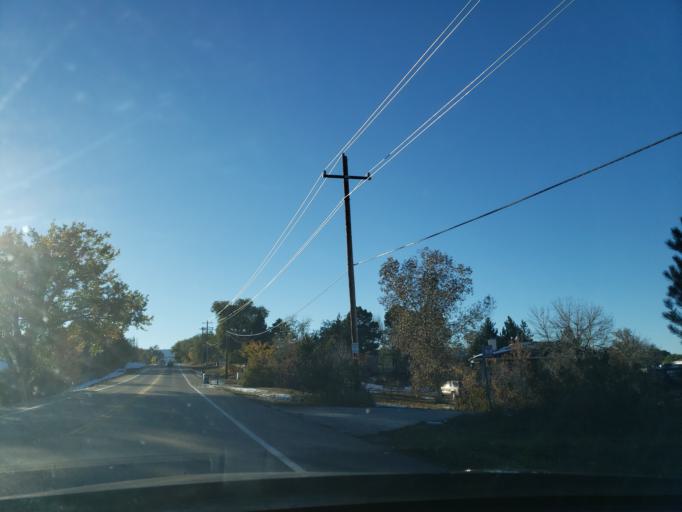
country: US
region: Colorado
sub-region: Larimer County
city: Fort Collins
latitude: 40.4948
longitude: -105.0727
